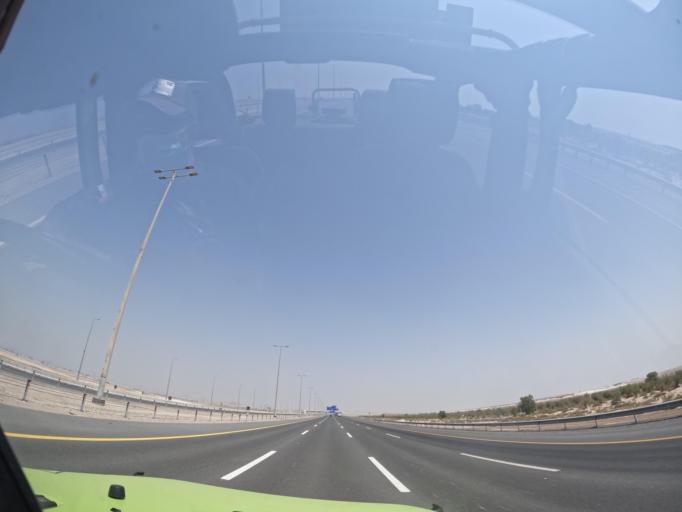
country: AE
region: Abu Dhabi
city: Abu Dhabi
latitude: 24.2747
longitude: 54.5147
